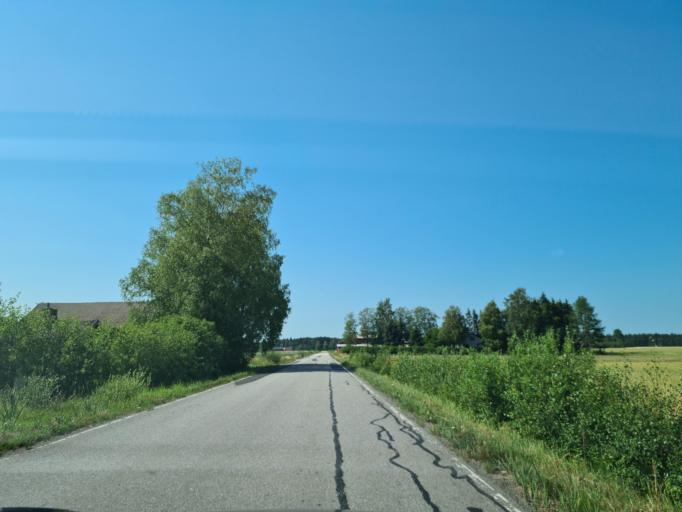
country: FI
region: Varsinais-Suomi
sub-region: Loimaa
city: Aura
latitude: 60.6043
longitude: 22.6383
